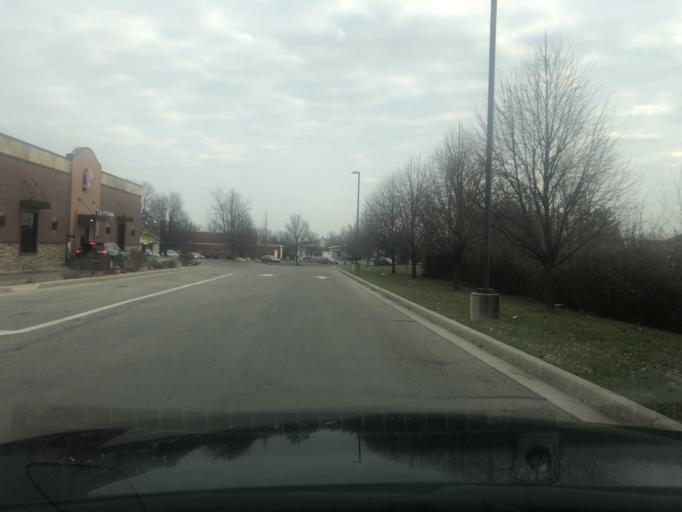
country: US
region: Michigan
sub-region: Wayne County
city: Belleville
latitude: 42.2251
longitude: -83.4858
